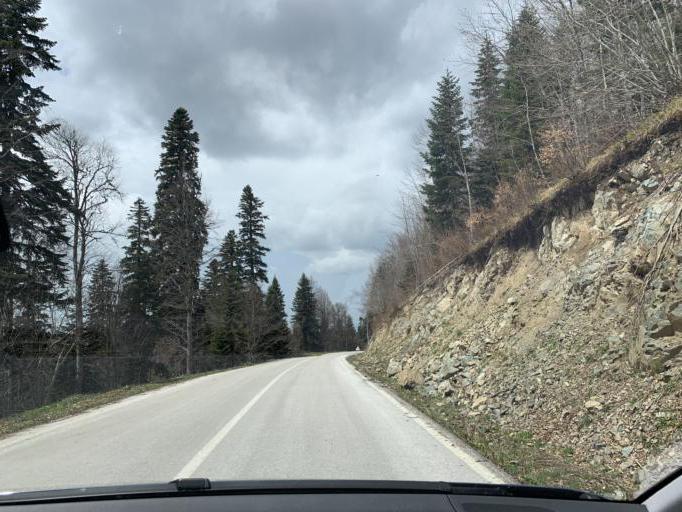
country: TR
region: Bolu
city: Bolu
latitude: 40.8926
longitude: 31.6735
